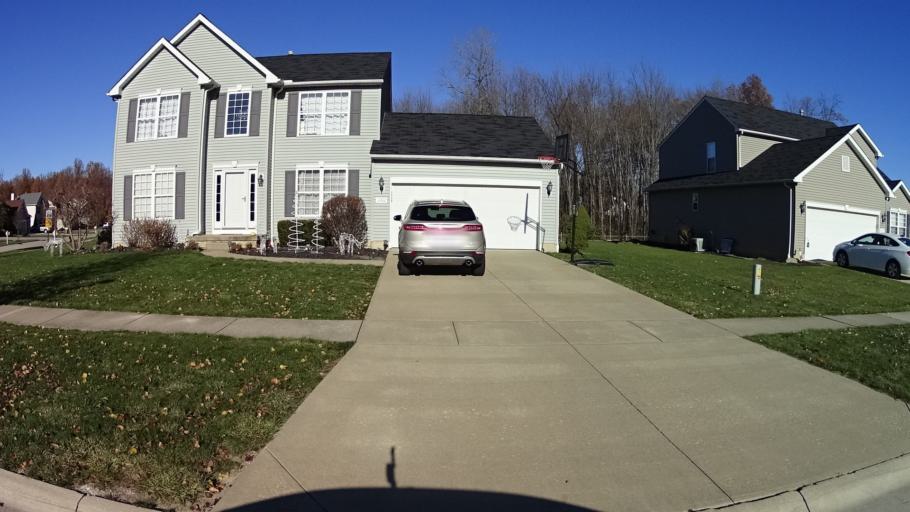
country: US
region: Ohio
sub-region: Lorain County
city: Avon Center
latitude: 41.4602
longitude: -81.9790
